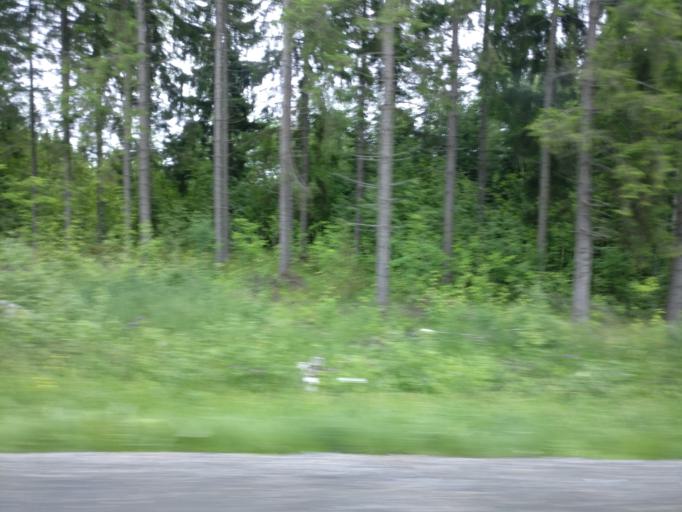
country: FI
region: Northern Savo
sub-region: Varkaus
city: Leppaevirta
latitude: 62.5913
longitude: 27.6052
